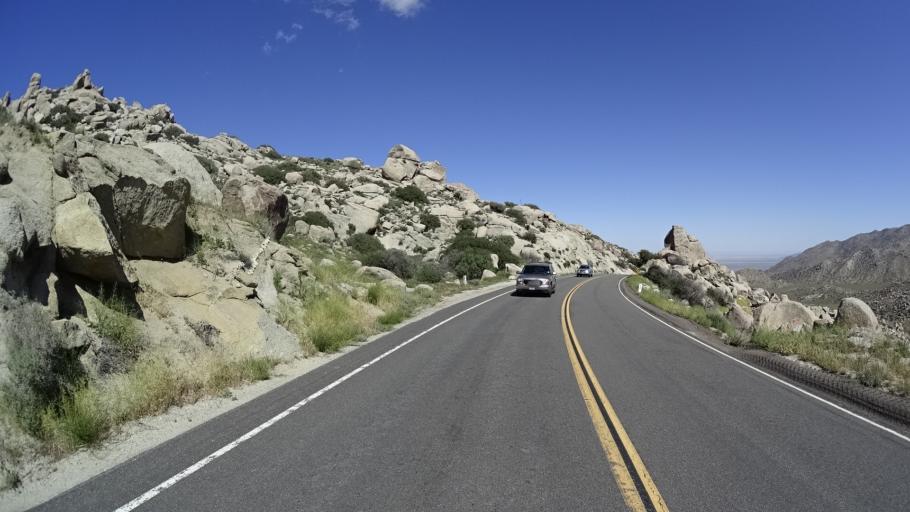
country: US
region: California
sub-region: San Diego County
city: Borrego Springs
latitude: 33.2143
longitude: -116.4685
